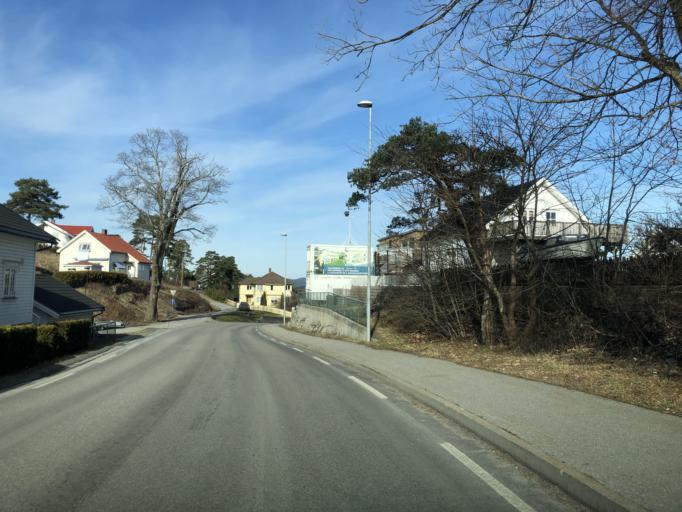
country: NO
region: Telemark
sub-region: Bamble
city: Langesund
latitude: 59.0062
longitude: 9.7442
